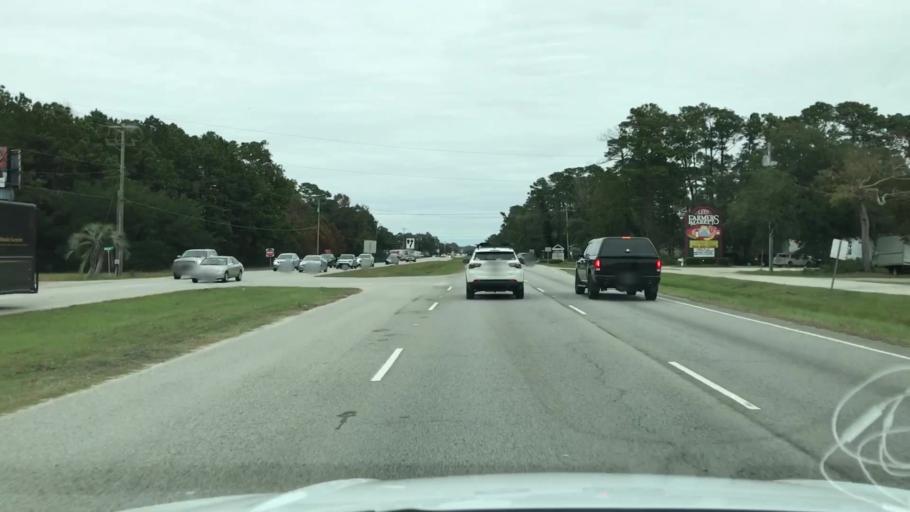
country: US
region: South Carolina
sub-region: Georgetown County
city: Murrells Inlet
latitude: 33.5417
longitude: -79.0537
